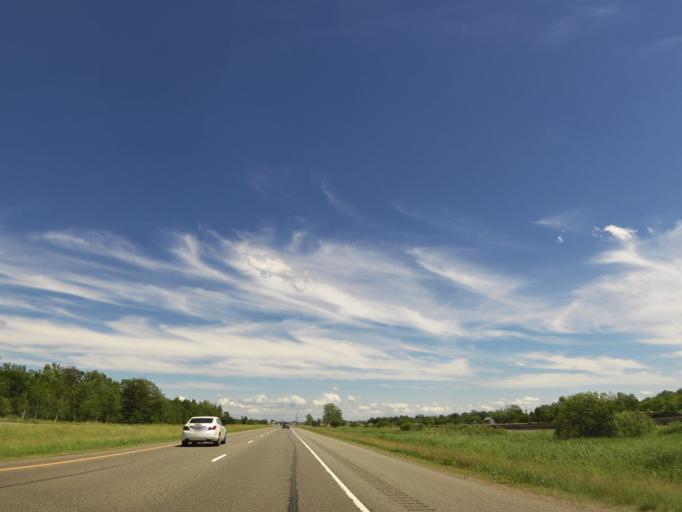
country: US
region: Minnesota
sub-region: Todd County
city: Staples
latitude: 46.3583
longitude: -94.8225
